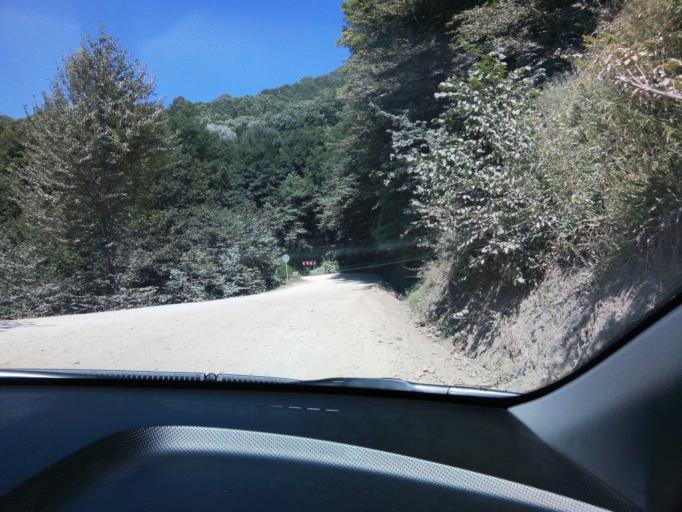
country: RU
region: Krasnodarskiy
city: Khadyzhensk
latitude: 44.3418
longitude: 39.2949
